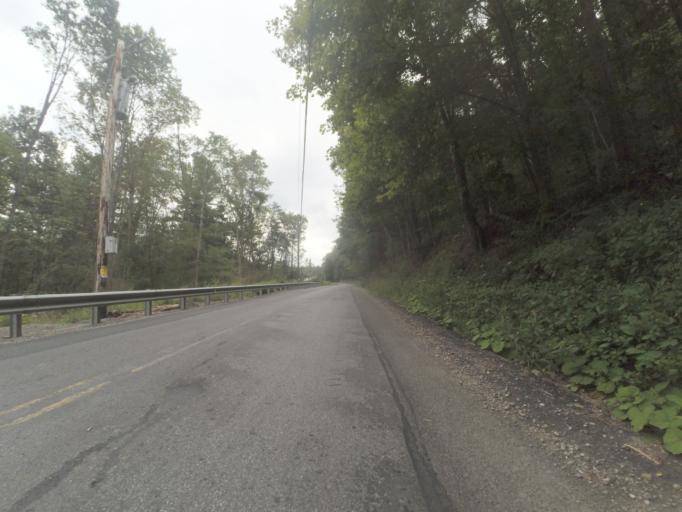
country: US
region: Pennsylvania
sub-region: Centre County
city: Zion
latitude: 41.0449
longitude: -77.6886
